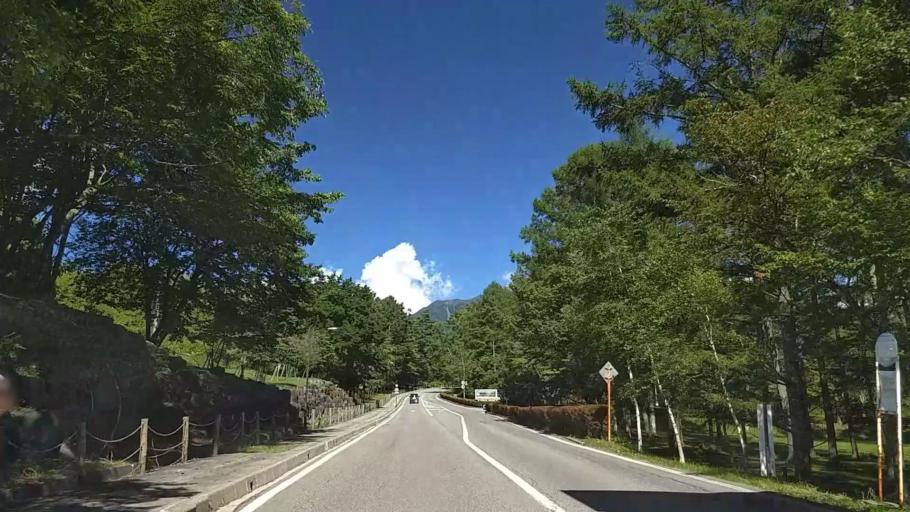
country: JP
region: Nagano
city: Chino
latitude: 36.0499
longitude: 138.2515
